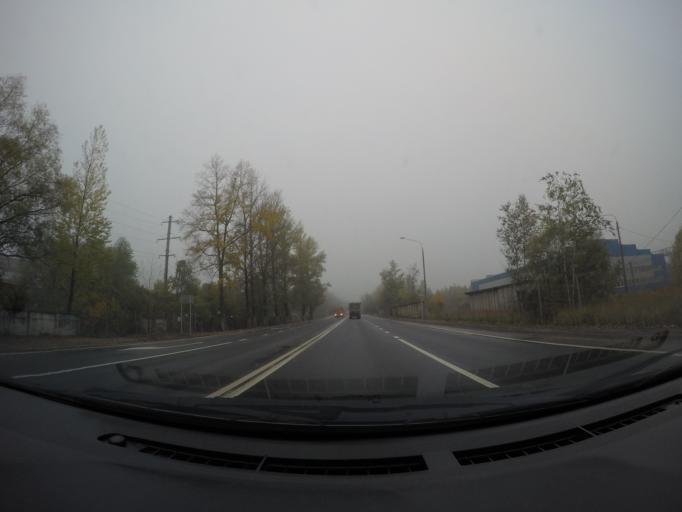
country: RU
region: Moskovskaya
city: Rumyantsevo
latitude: 55.8754
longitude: 36.5568
